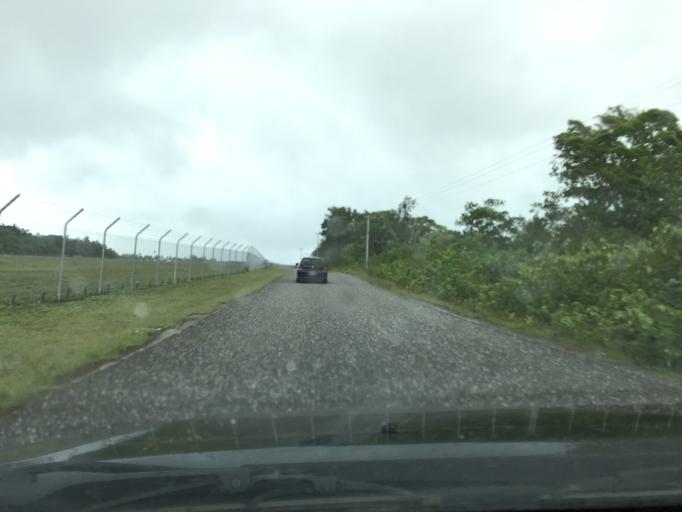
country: SB
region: Western Province
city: Gizo
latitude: -8.3262
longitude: 157.2624
